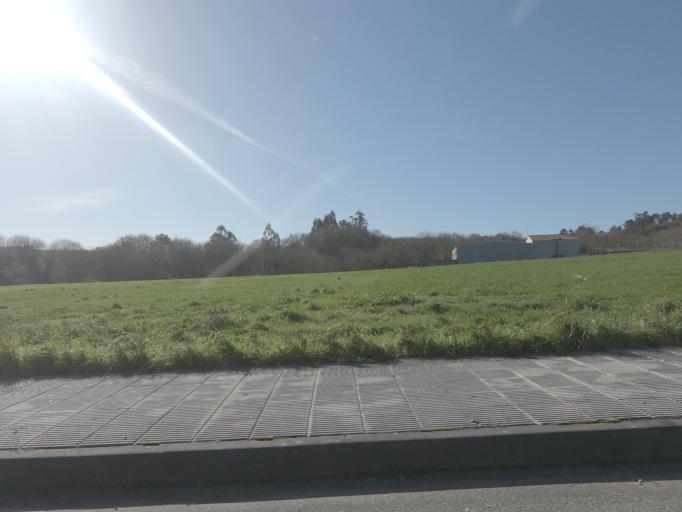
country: ES
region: Galicia
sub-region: Provincia de Pontevedra
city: Silleda
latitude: 42.6954
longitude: -8.2384
